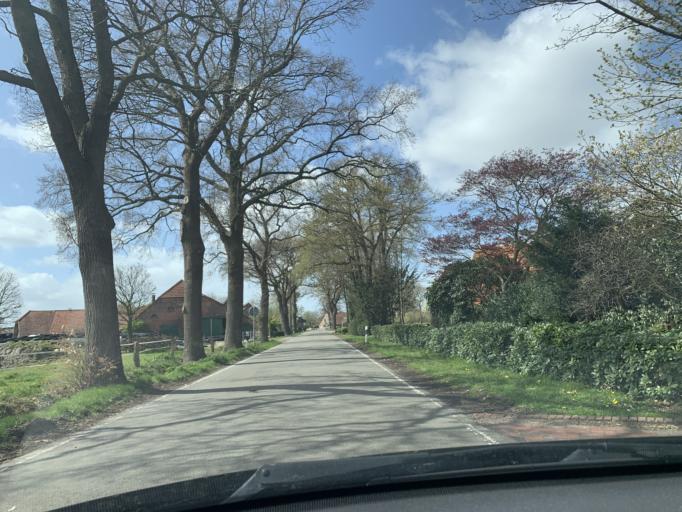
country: DE
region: Lower Saxony
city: Westerstede
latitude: 53.3059
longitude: 7.9451
